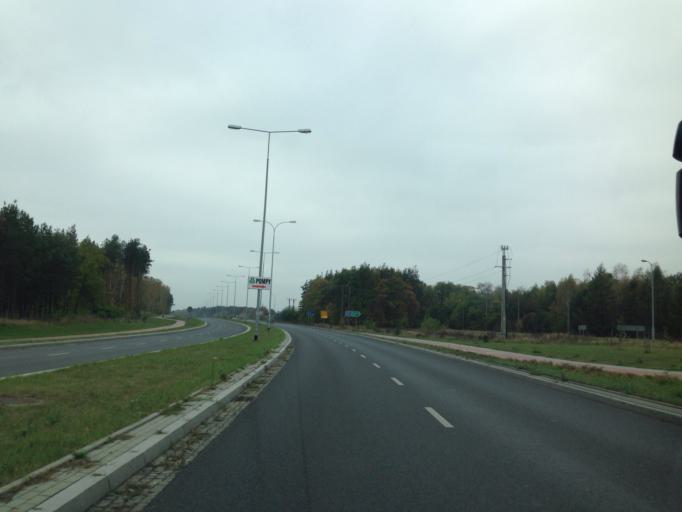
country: PL
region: Kujawsko-Pomorskie
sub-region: Grudziadz
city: Grudziadz
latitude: 53.4664
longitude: 18.7513
